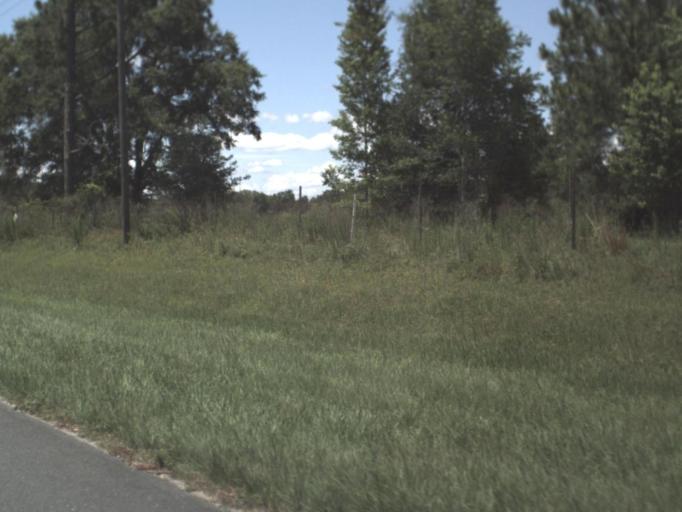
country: US
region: Florida
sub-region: Lafayette County
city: Mayo
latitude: 30.1163
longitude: -83.2592
